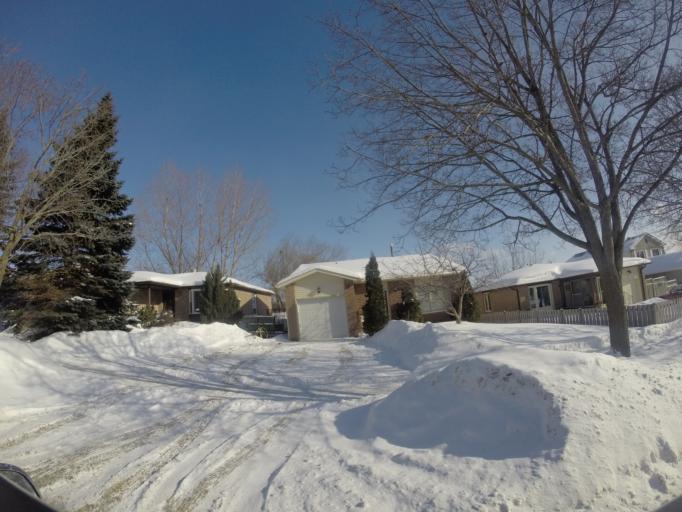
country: CA
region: Ontario
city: Barrie
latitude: 44.3858
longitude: -79.7213
